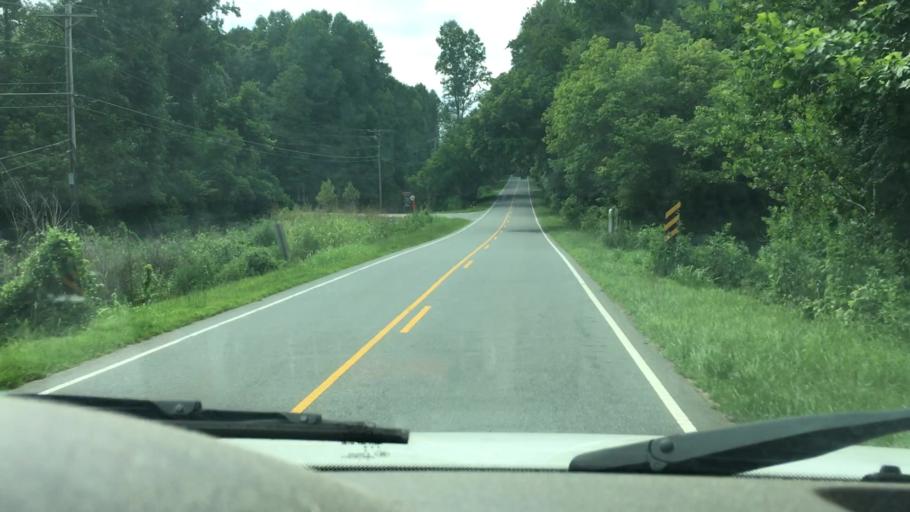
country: US
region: North Carolina
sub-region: Gaston County
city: Davidson
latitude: 35.4727
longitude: -80.7922
